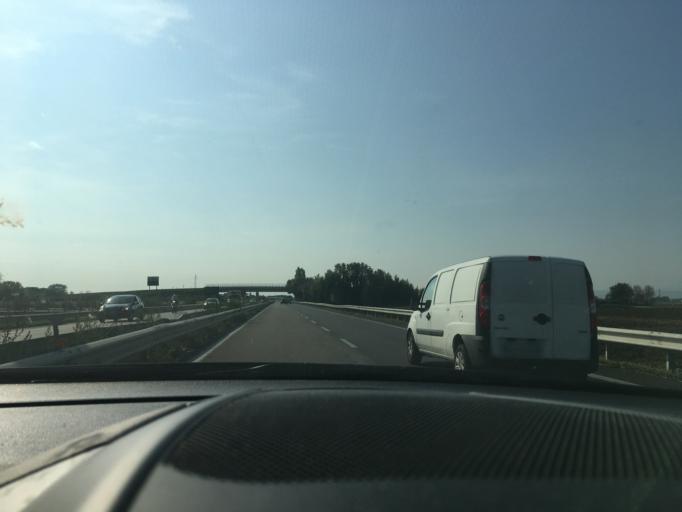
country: IT
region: Emilia-Romagna
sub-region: Provincia di Rimini
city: Bellaria-Igea Marina
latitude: 44.1217
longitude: 12.4724
